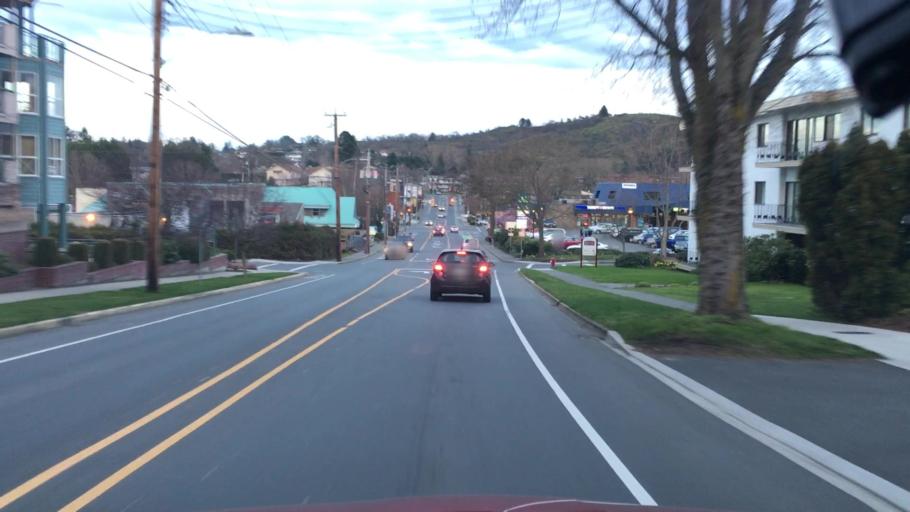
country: CA
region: British Columbia
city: Oak Bay
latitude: 48.4623
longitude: -123.3358
